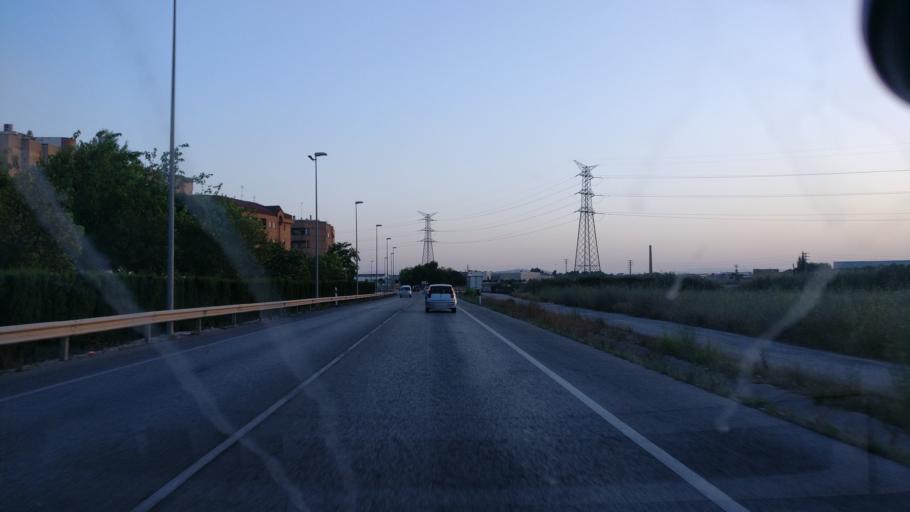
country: ES
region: Valencia
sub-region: Provincia de Valencia
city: Xirivella
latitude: 39.4667
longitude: -0.4358
